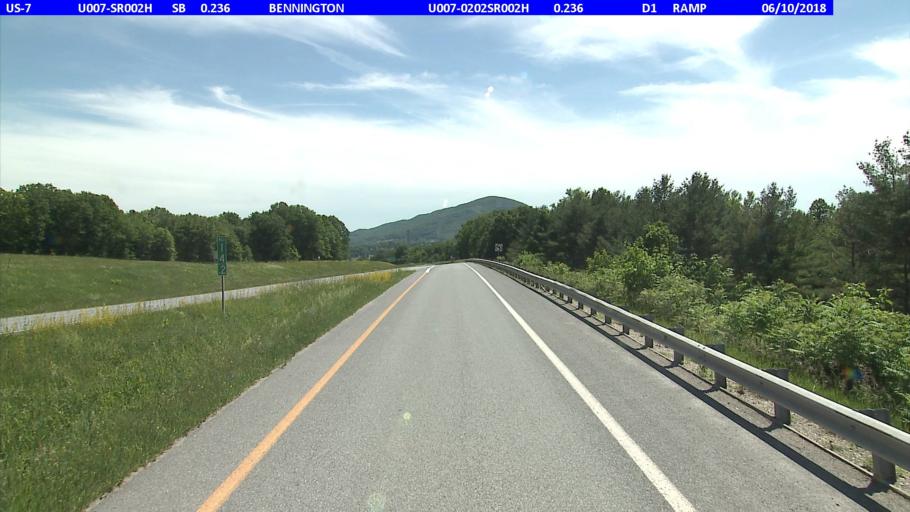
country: US
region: Vermont
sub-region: Bennington County
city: North Bennington
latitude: 42.9209
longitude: -73.2074
